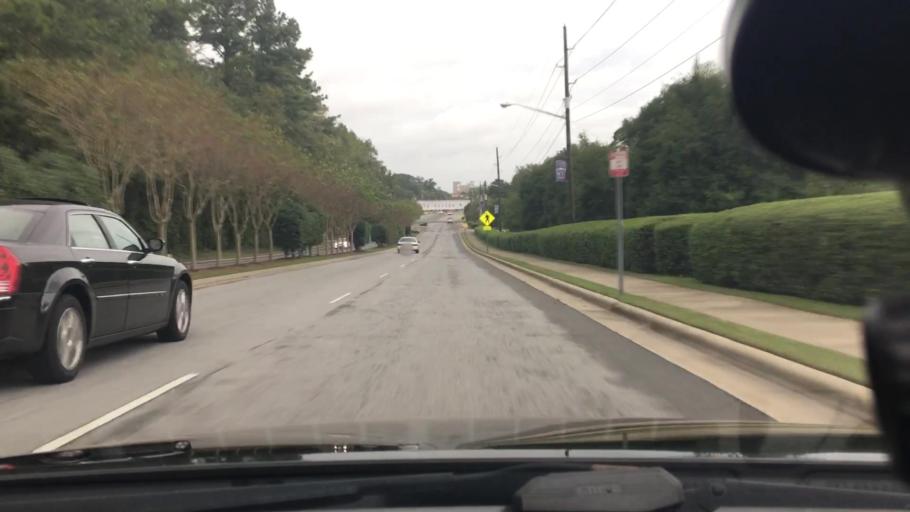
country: US
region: North Carolina
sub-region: Pitt County
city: Greenville
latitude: 35.5968
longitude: -77.3698
